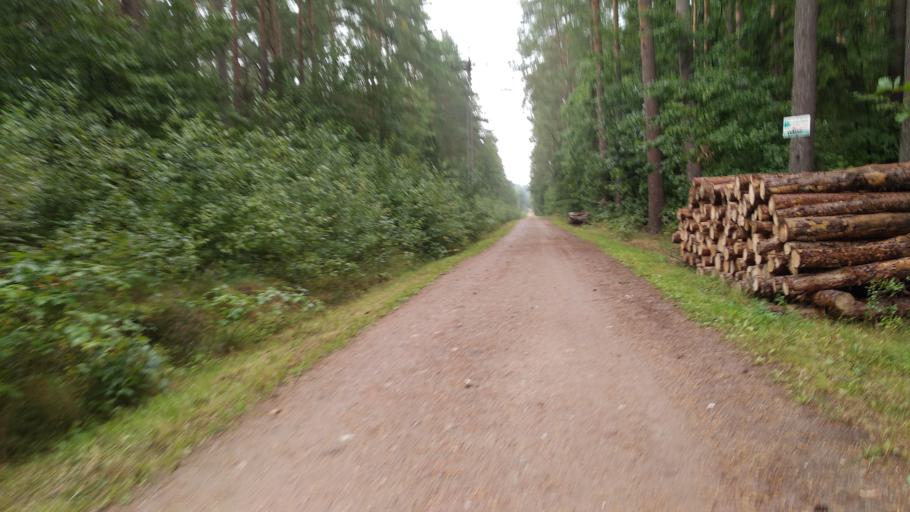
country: PL
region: Pomeranian Voivodeship
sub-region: Powiat wejherowski
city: Goscicino
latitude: 54.6182
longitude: 18.1566
